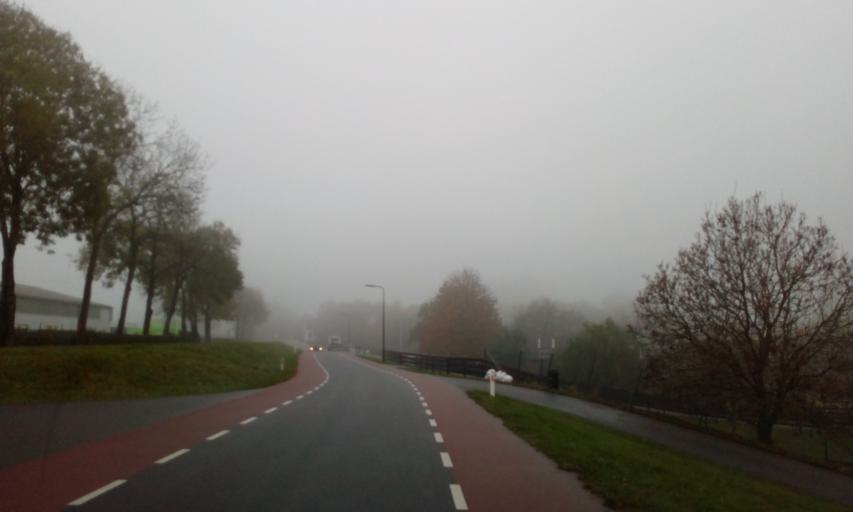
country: NL
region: South Holland
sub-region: Molenwaard
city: Liesveld
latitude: 51.9237
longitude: 4.7940
